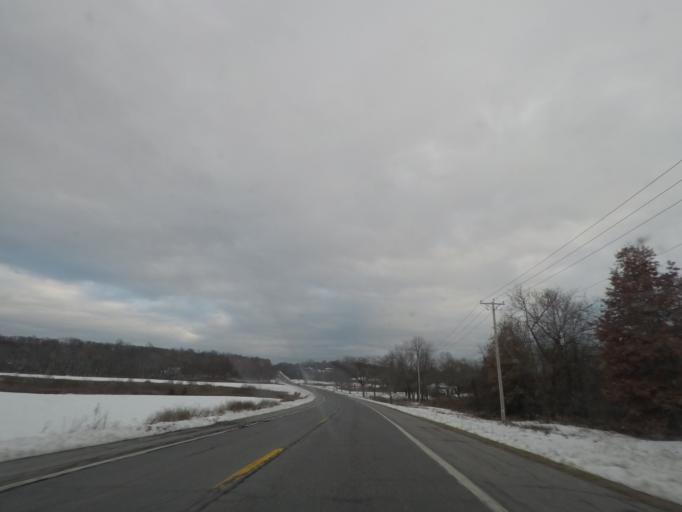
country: US
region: New York
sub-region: Ulster County
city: Plattekill
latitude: 41.6420
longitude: -74.1111
